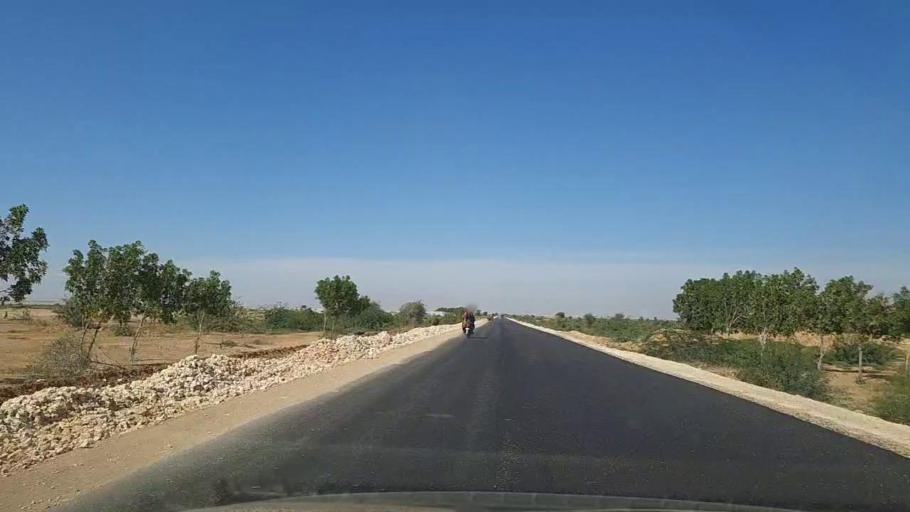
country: PK
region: Sindh
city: Kotri
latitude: 25.2518
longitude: 68.2271
